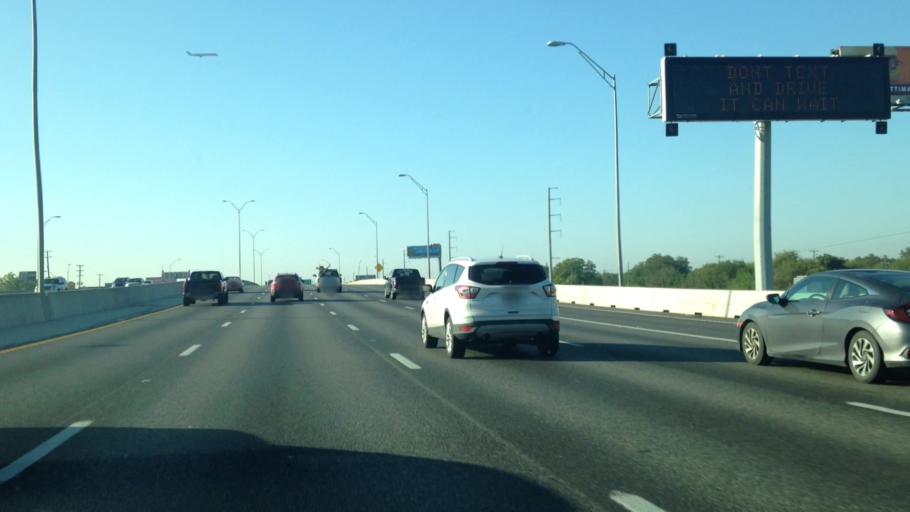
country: US
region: Texas
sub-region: Bexar County
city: Windcrest
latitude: 29.4984
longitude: -98.4006
